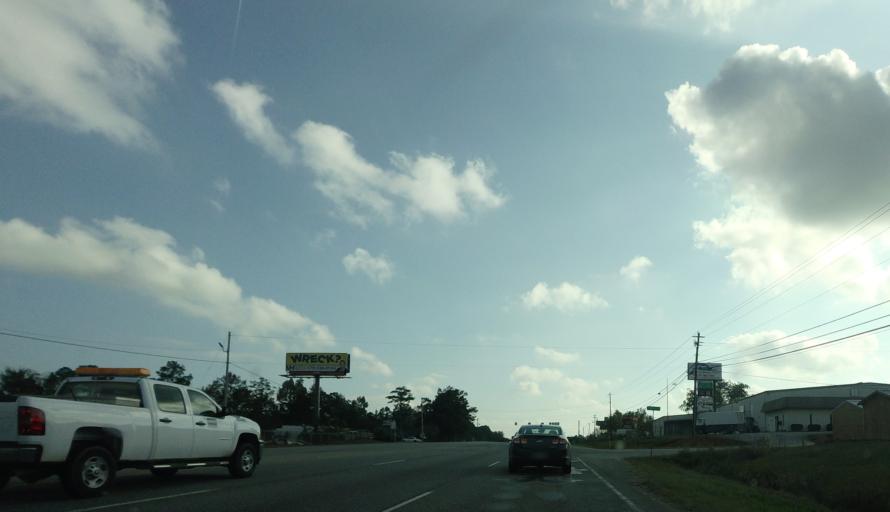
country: US
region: Georgia
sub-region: Houston County
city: Centerville
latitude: 32.7338
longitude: -83.6558
